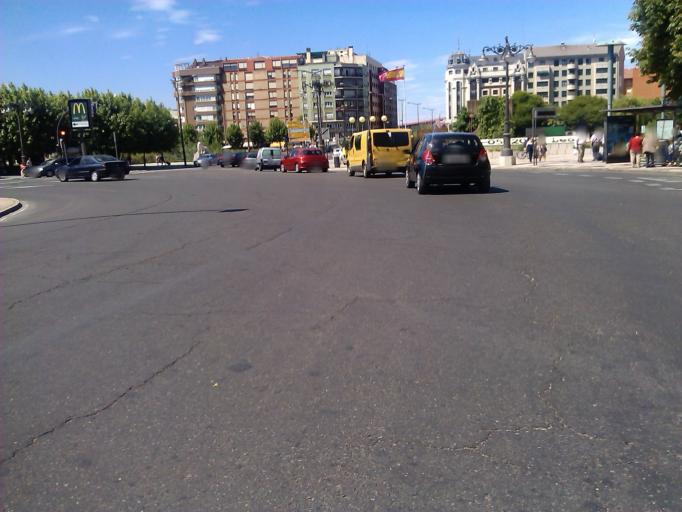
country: ES
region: Castille and Leon
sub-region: Provincia de Leon
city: Leon
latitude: 42.5965
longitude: -5.5782
